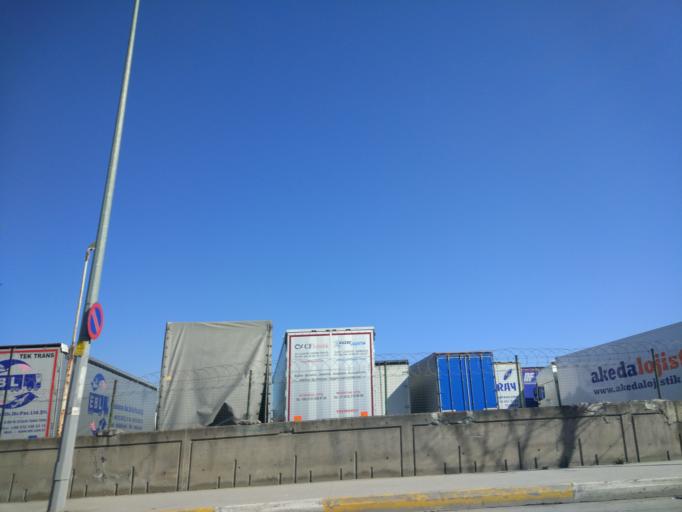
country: TR
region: Istanbul
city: Mahmutbey
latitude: 41.0216
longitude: 28.8055
